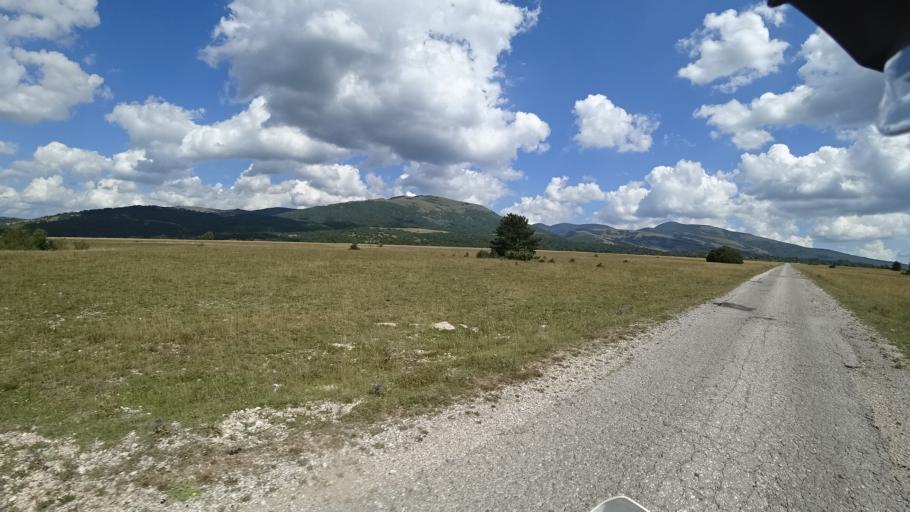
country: HR
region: Zadarska
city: Gracac
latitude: 44.5433
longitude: 15.7903
